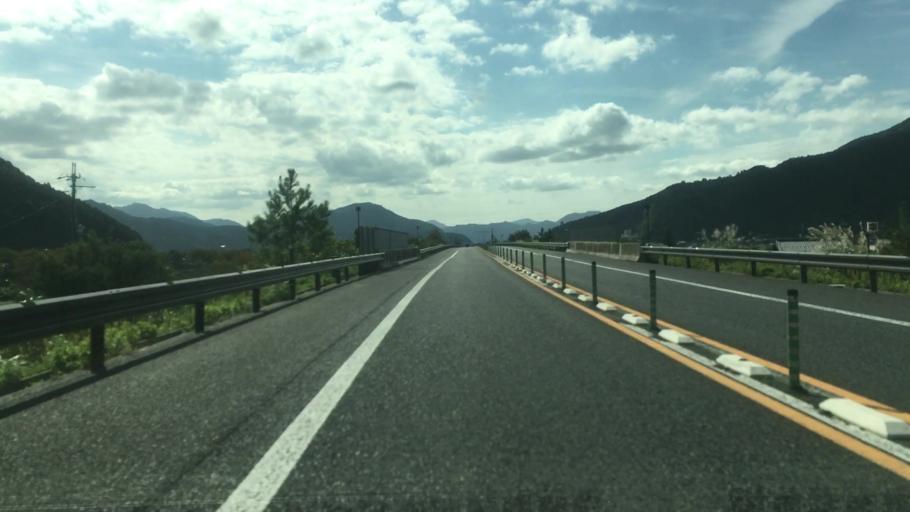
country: JP
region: Kyoto
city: Fukuchiyama
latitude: 35.2197
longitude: 135.0346
